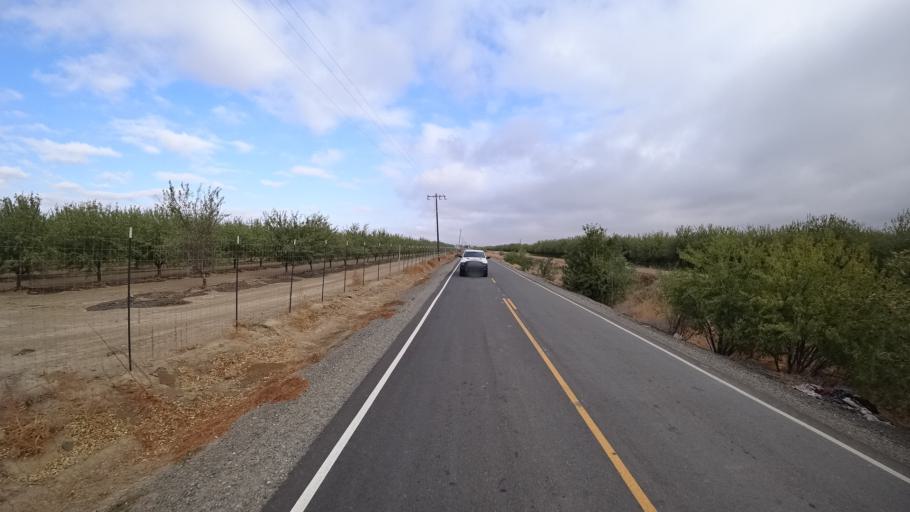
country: US
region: California
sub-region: Yolo County
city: Esparto
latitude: 38.7601
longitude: -122.0442
